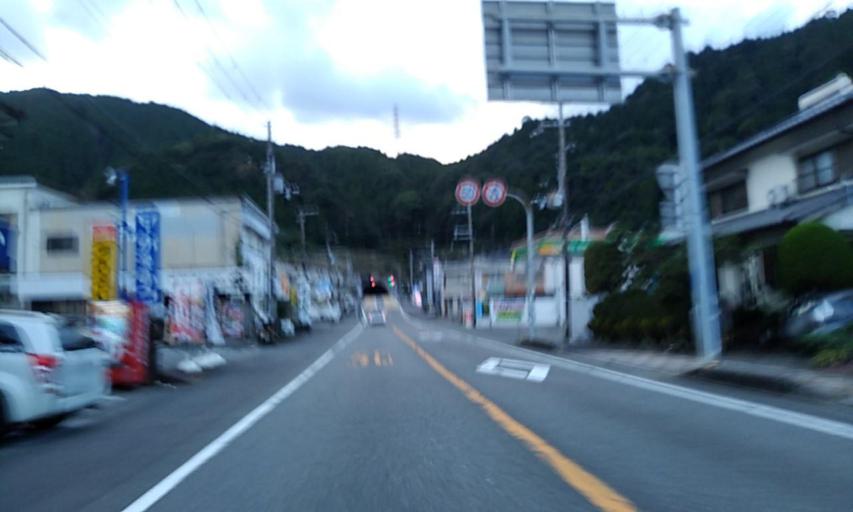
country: JP
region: Wakayama
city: Shingu
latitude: 33.7192
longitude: 135.9817
